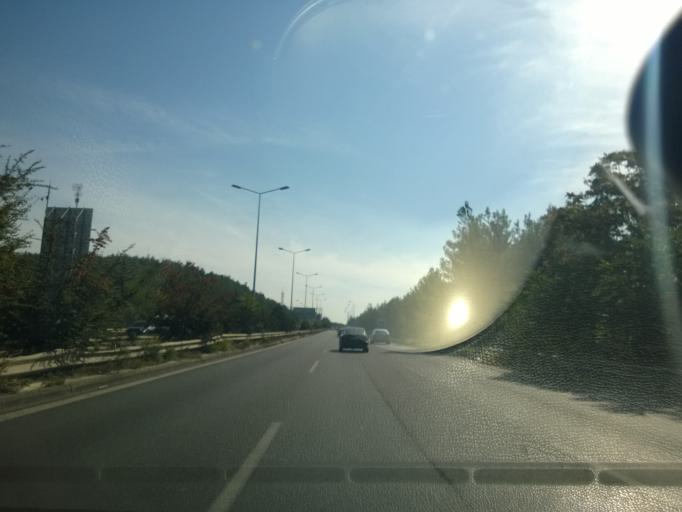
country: GR
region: Central Macedonia
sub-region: Nomos Thessalonikis
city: Agios Pavlos
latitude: 40.6491
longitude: 22.9671
